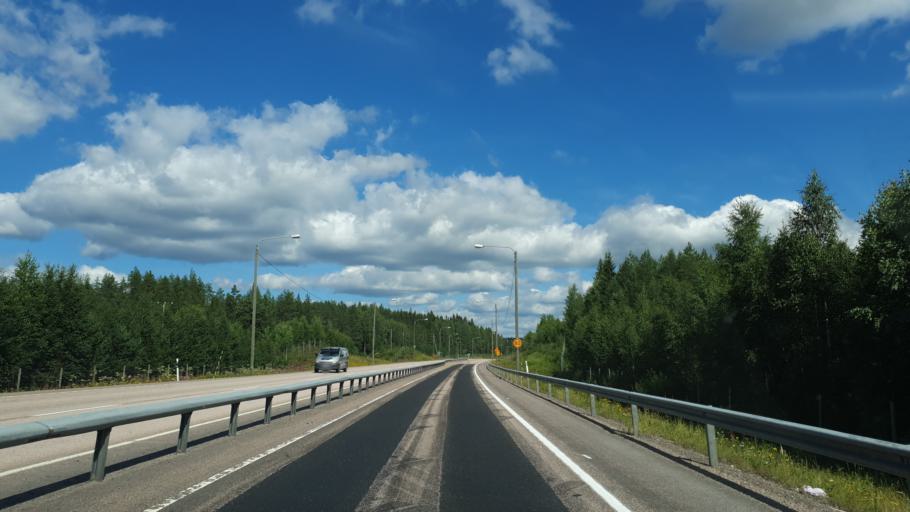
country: FI
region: Central Finland
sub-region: Jaemsae
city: Jaemsae
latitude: 61.7964
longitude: 24.9460
